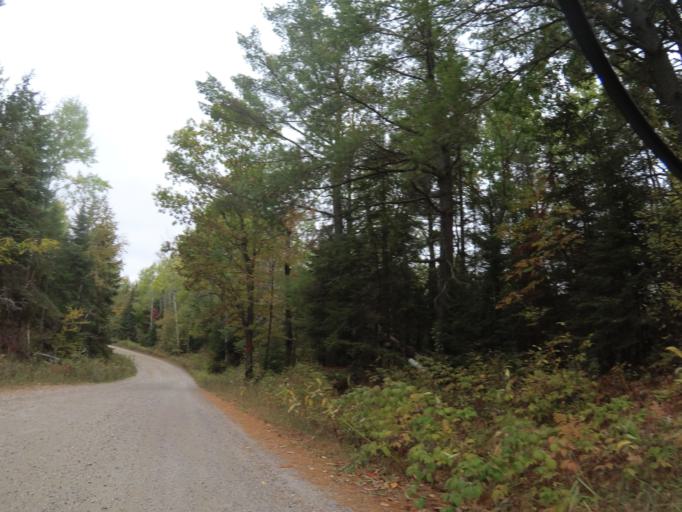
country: CA
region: Ontario
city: Renfrew
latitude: 45.2931
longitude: -77.0240
